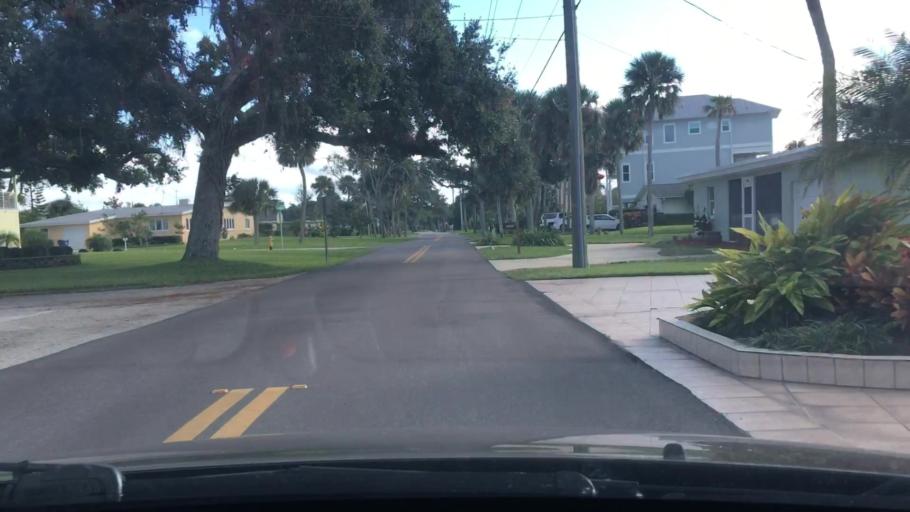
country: US
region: Florida
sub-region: Volusia County
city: Ormond-by-the-Sea
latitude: 29.3683
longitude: -81.0816
